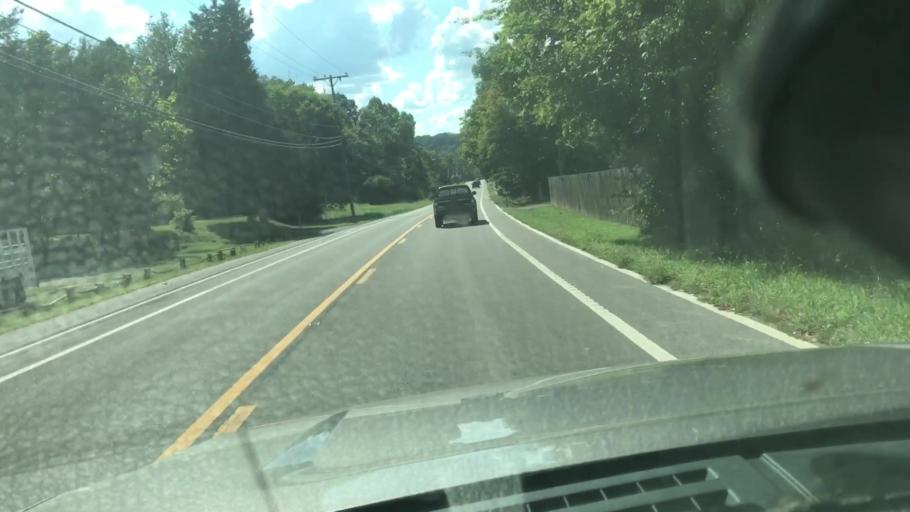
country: US
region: Tennessee
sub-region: Cheatham County
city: Pegram
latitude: 36.0270
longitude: -87.0138
